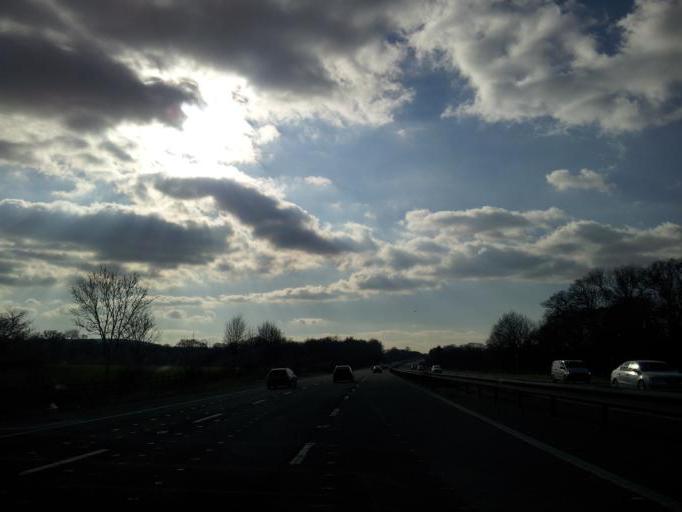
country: GB
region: England
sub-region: Somerset
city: Taunton
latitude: 50.9746
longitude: -3.1613
